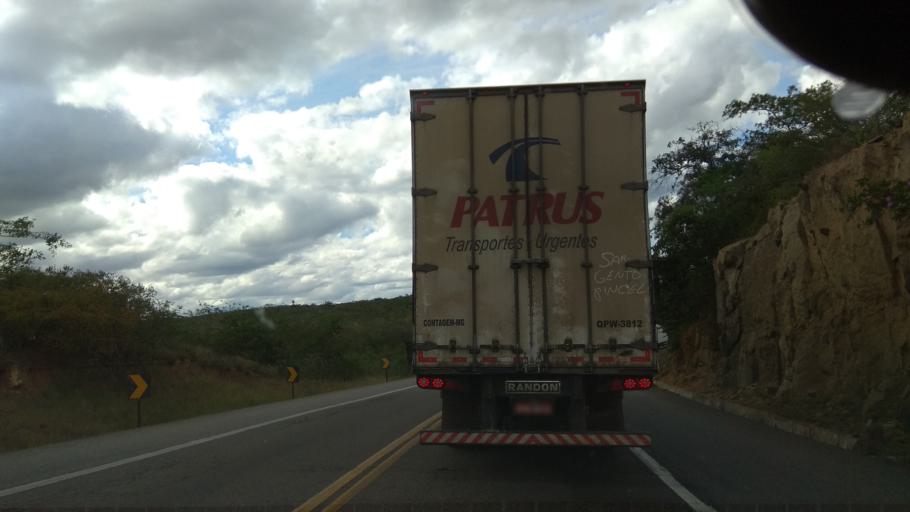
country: BR
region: Bahia
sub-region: Santa Ines
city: Santa Ines
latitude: -12.9950
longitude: -39.9532
